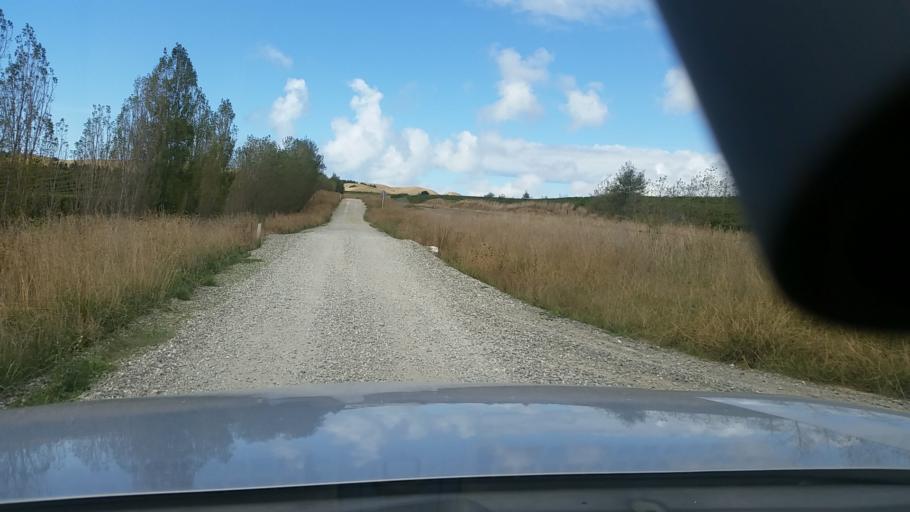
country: NZ
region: Marlborough
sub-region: Marlborough District
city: Blenheim
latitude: -41.6867
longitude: 174.1312
